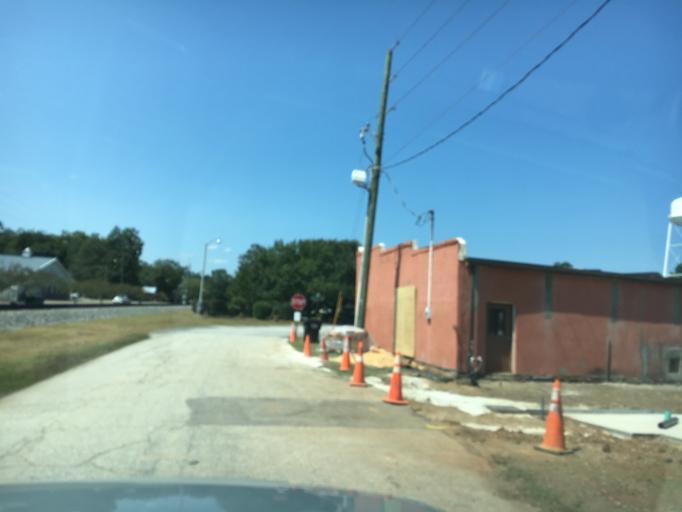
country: US
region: South Carolina
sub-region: Lexington County
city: Batesburg
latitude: 33.8449
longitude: -81.6602
